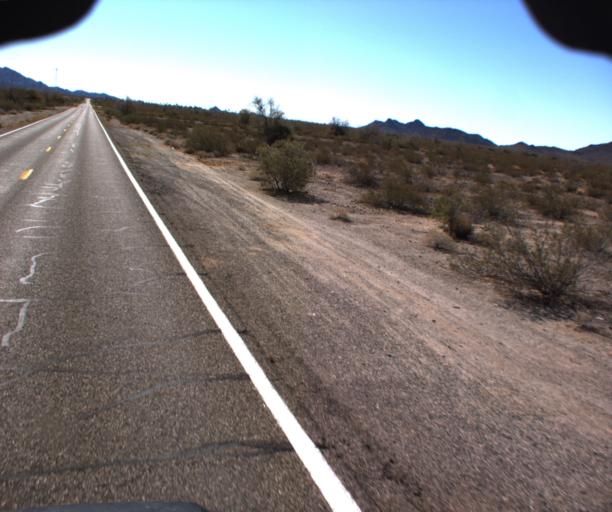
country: US
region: Arizona
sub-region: La Paz County
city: Salome
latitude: 33.7319
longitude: -113.7219
